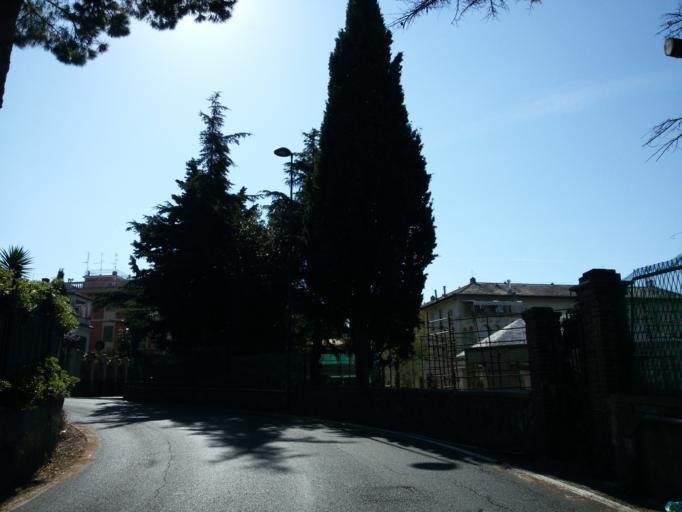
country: IT
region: Liguria
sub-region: Provincia di Genova
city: Bogliasco
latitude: 44.3883
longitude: 9.0041
